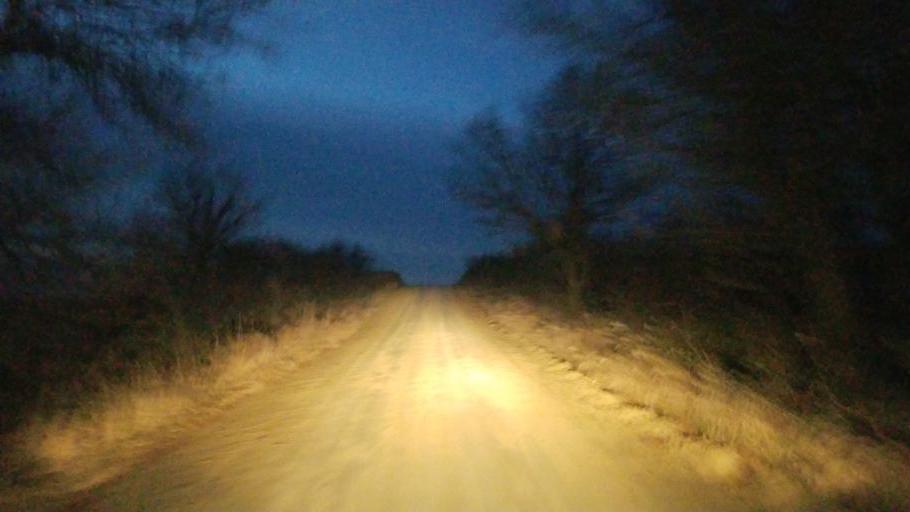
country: US
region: Nebraska
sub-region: Knox County
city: Center
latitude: 42.5729
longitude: -97.7984
